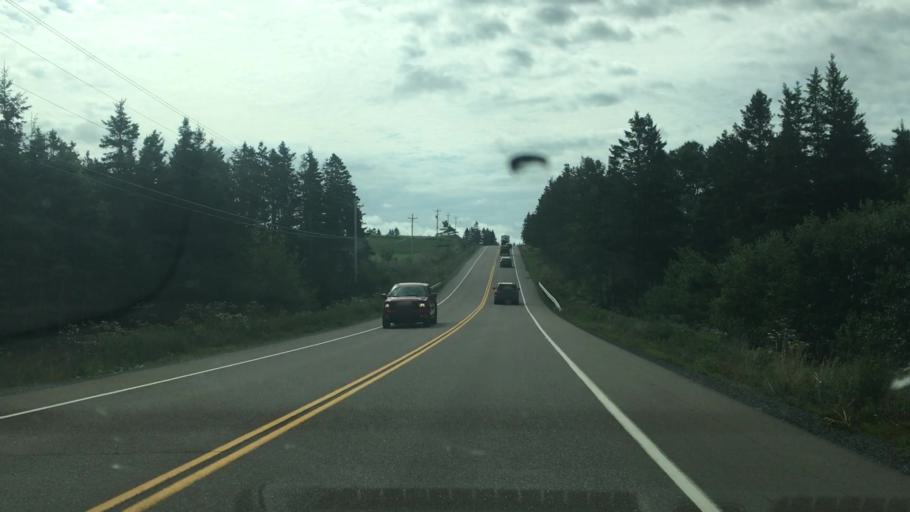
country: CA
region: Nova Scotia
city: Princeville
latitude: 45.7001
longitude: -60.7370
